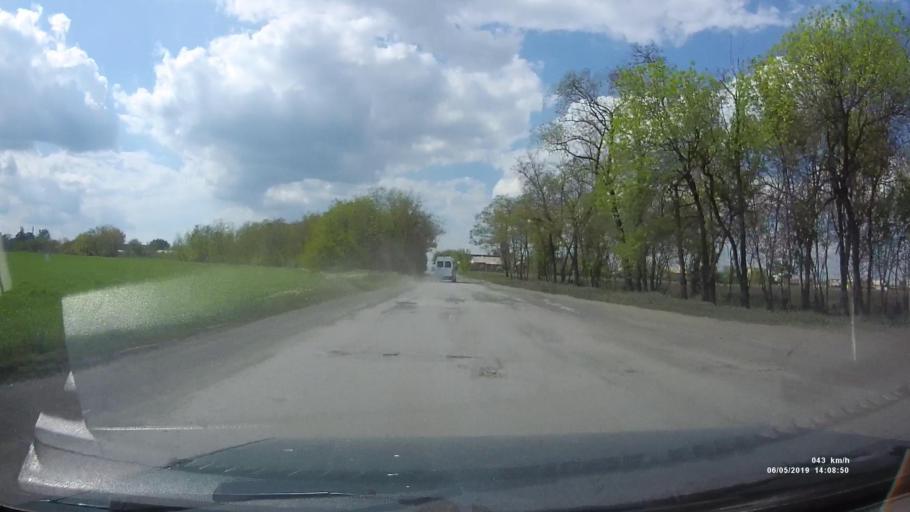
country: RU
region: Rostov
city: Shakhty
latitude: 47.6845
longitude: 40.2947
